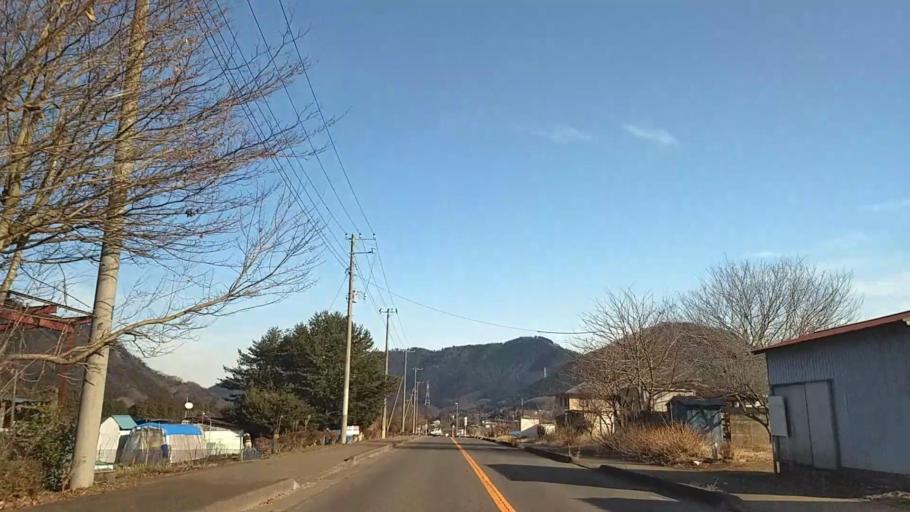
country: JP
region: Yamanashi
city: Uenohara
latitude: 35.5644
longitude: 139.1926
